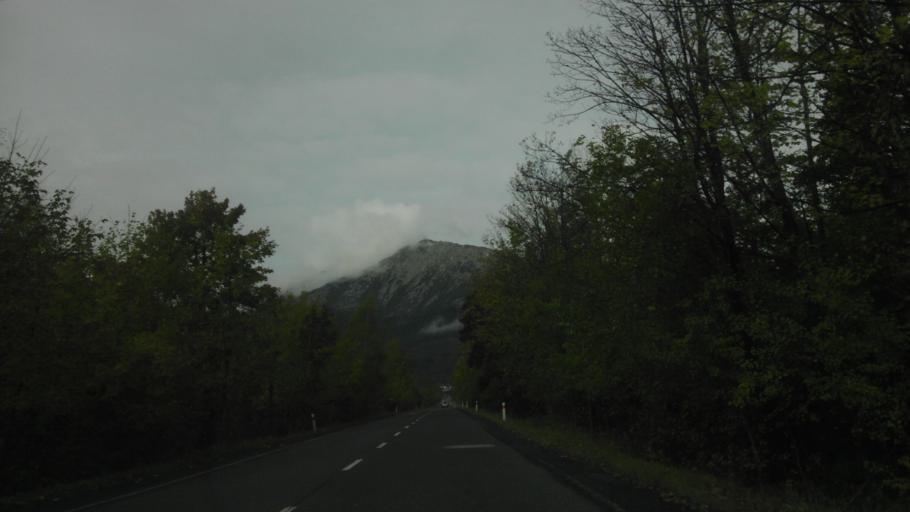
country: SK
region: Presovsky
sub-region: Okres Poprad
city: Vysoke Tatry
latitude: 49.1261
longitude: 20.2432
